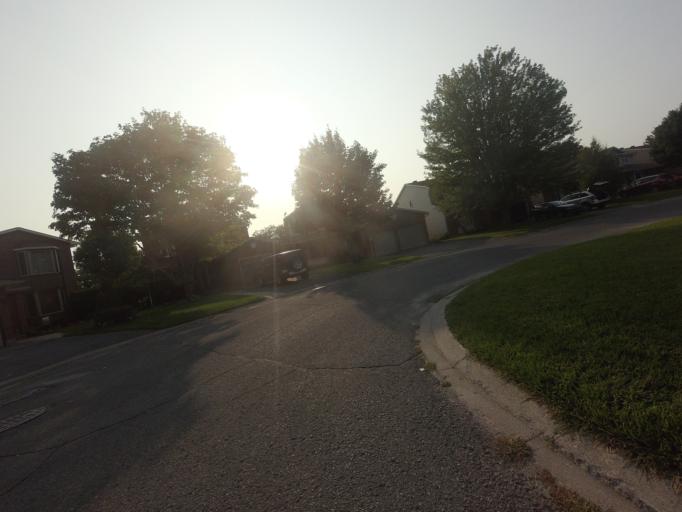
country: CA
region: Ontario
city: Bells Corners
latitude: 45.3364
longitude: -75.7648
